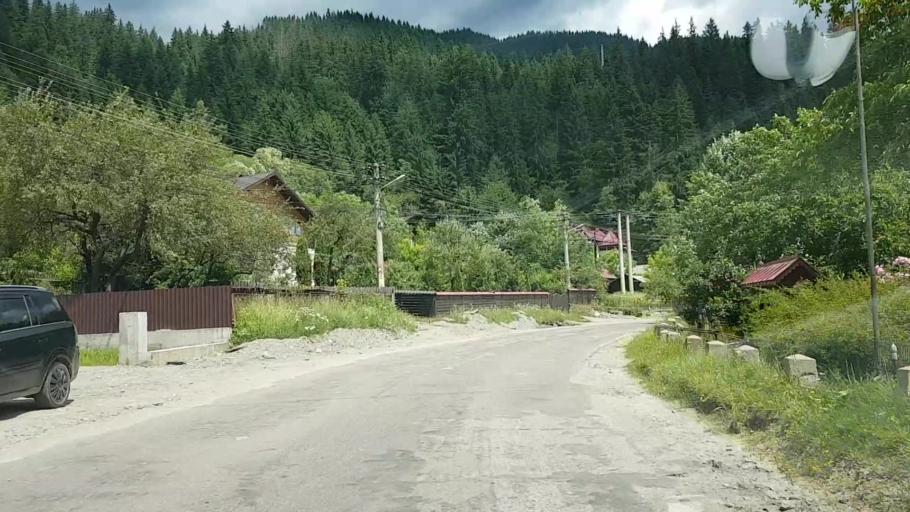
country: RO
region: Suceava
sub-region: Comuna Brosteni
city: Brosteni
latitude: 47.2430
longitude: 25.7026
